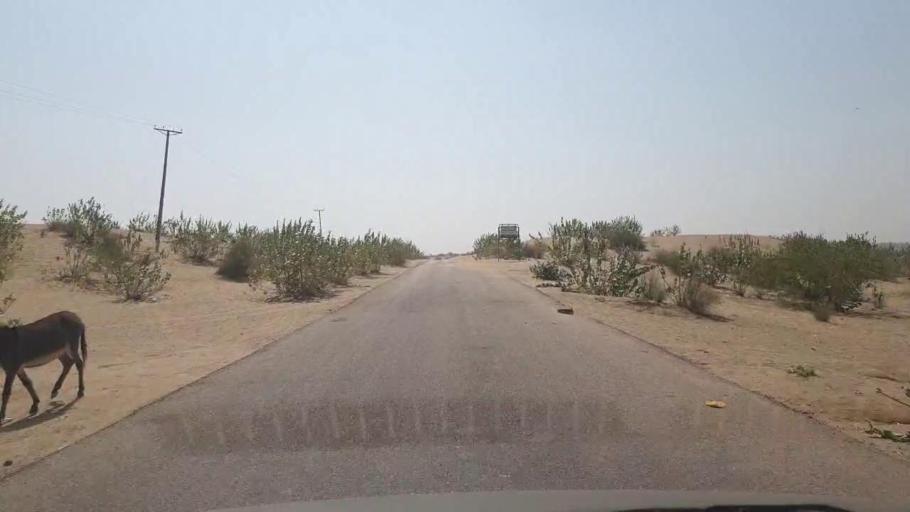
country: PK
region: Sindh
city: Chor
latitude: 25.6638
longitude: 70.1670
